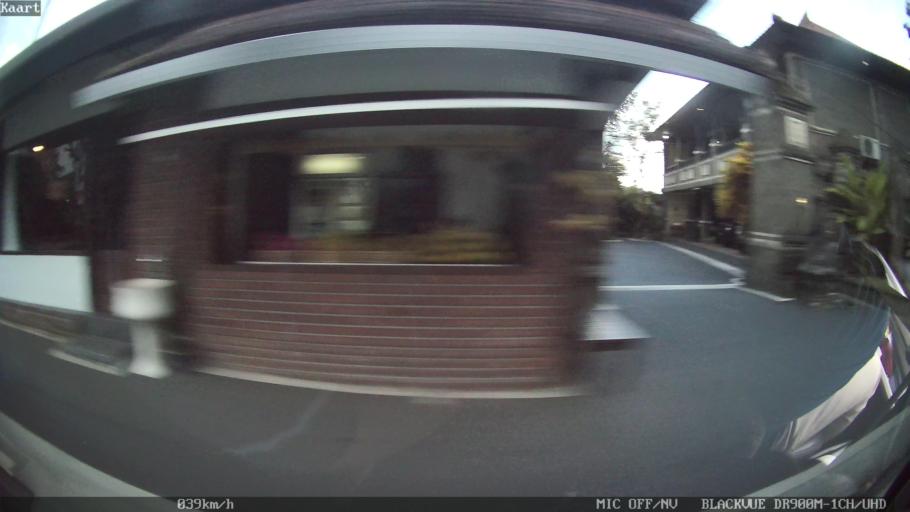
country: ID
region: Bali
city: Banjar Tebongkang
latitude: -8.5242
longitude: 115.2427
